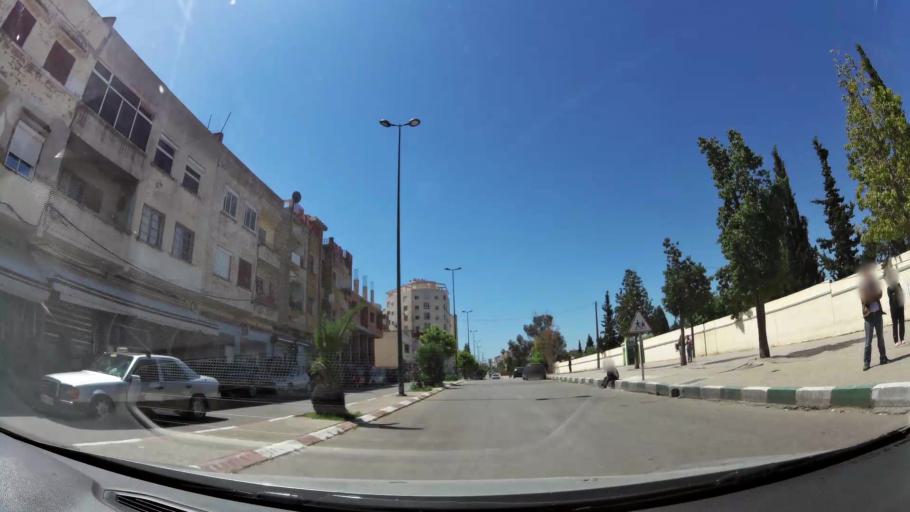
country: MA
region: Meknes-Tafilalet
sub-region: Meknes
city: Meknes
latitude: 33.9067
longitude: -5.5326
